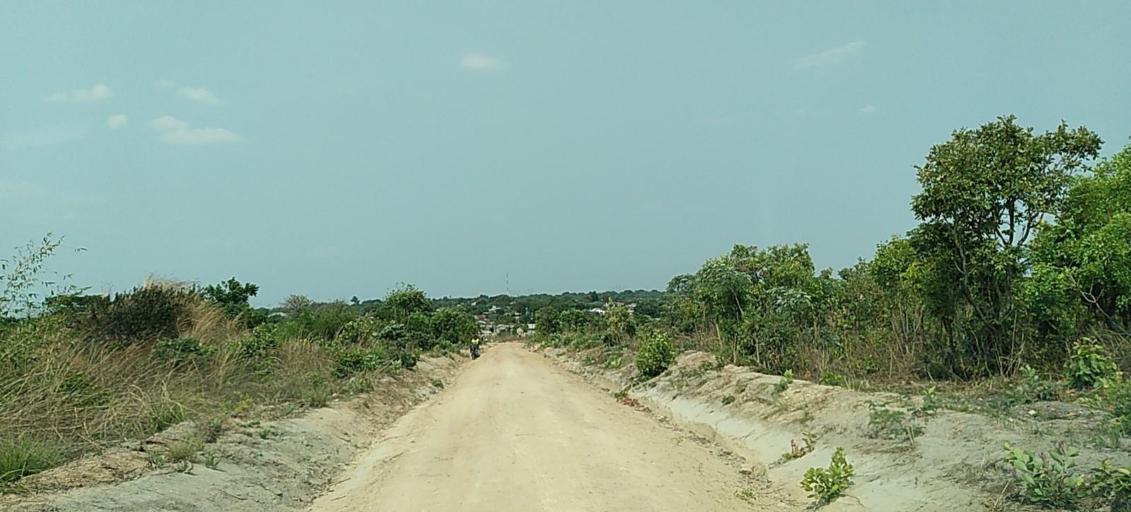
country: ZM
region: Copperbelt
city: Chambishi
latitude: -12.6239
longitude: 28.0826
